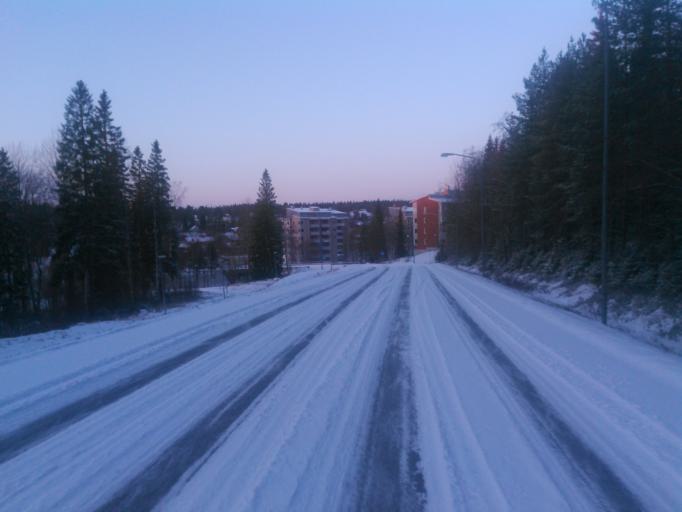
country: SE
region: Vaesterbotten
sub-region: Umea Kommun
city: Umea
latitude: 63.8241
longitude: 20.3135
